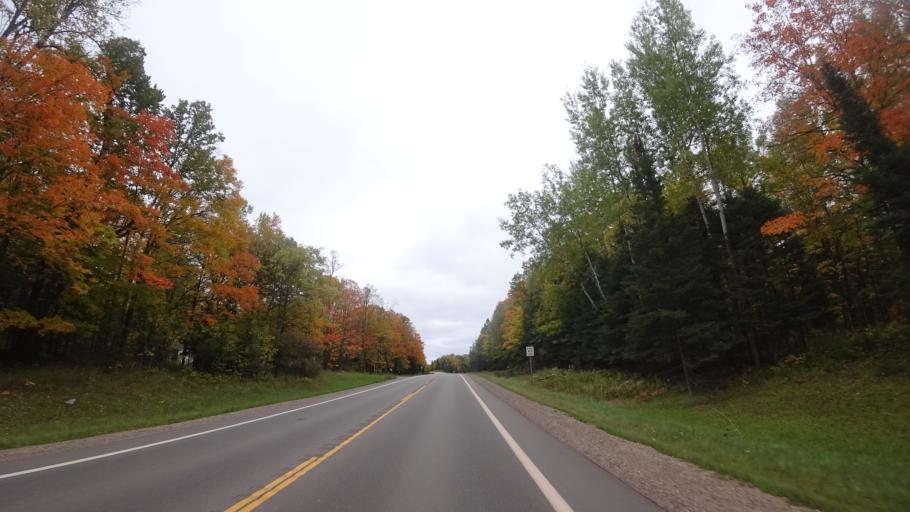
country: US
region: Michigan
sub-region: Iron County
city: Crystal Falls
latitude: 46.1722
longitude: -88.0601
